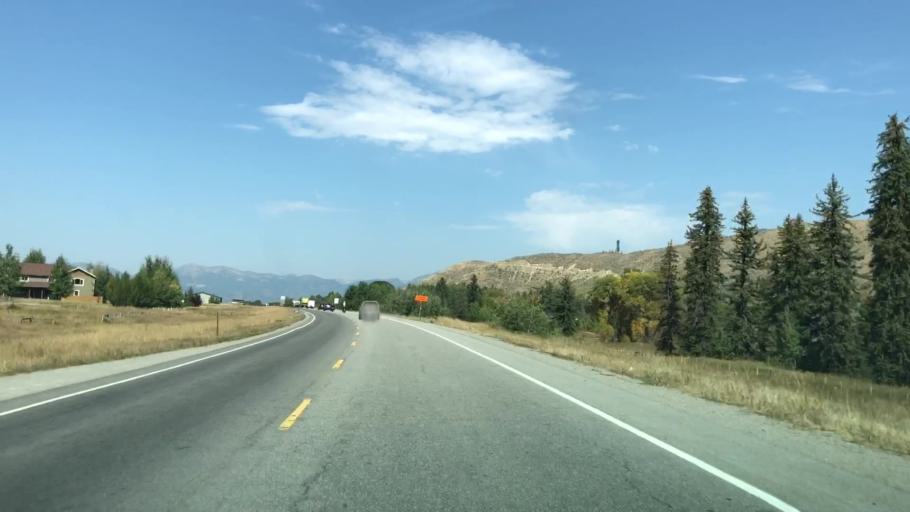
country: US
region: Wyoming
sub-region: Teton County
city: South Park
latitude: 43.3622
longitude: -110.7280
